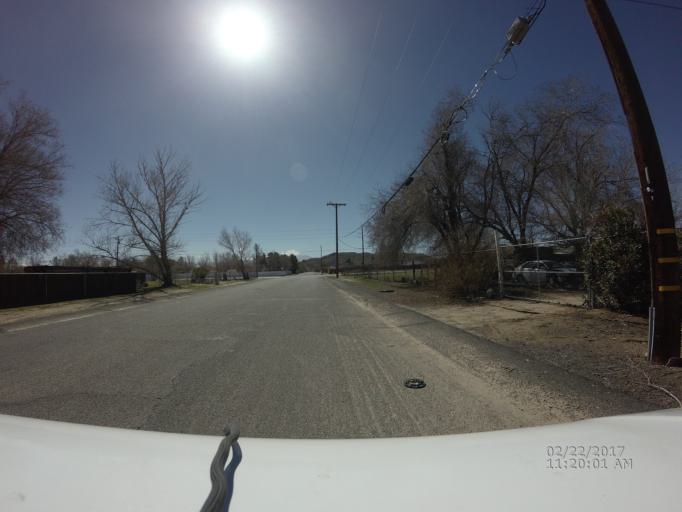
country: US
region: California
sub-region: Los Angeles County
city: Lake Los Angeles
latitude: 34.6172
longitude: -117.8139
